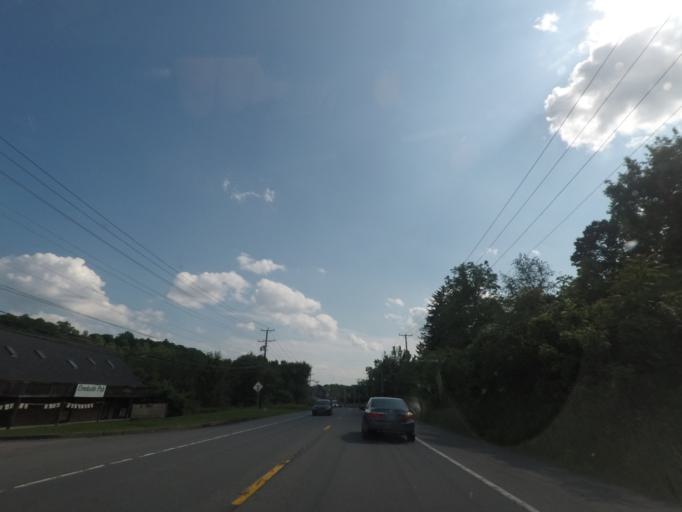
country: US
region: New York
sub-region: Ulster County
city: Marlboro
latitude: 41.5807
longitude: -73.9877
